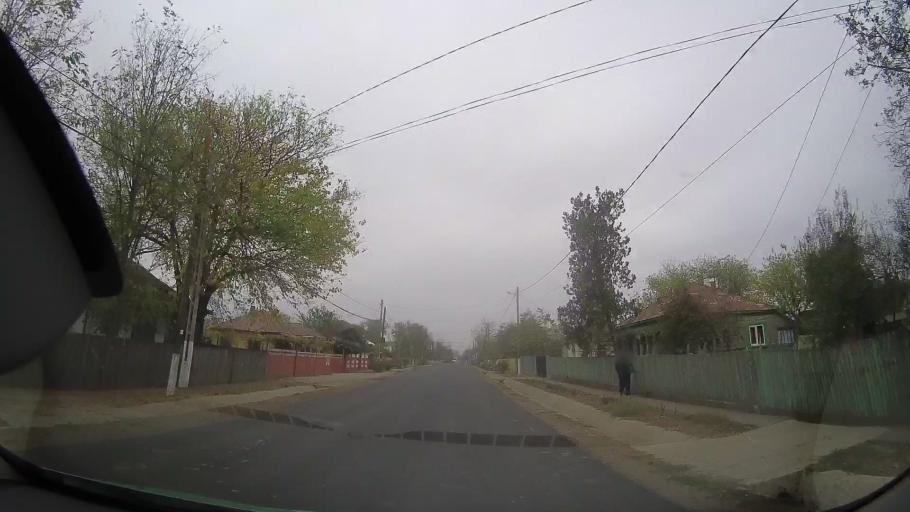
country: RO
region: Braila
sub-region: Comuna Rosiori
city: Rosiori
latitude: 44.8088
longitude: 27.3856
